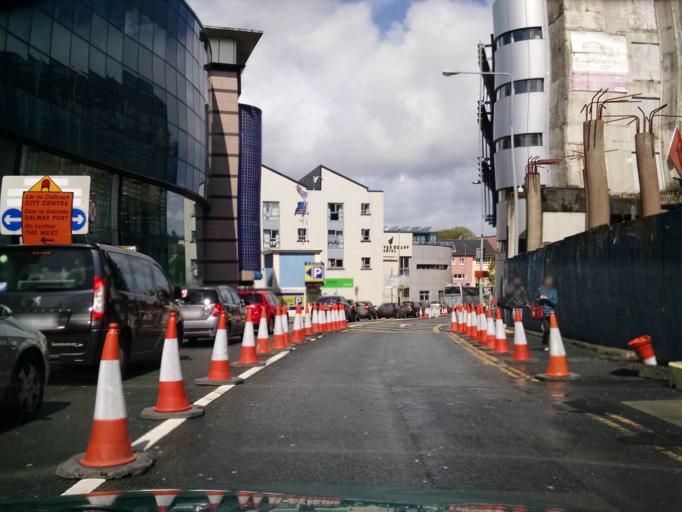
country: IE
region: Connaught
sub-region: County Galway
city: Gaillimh
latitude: 53.2742
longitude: -9.0452
